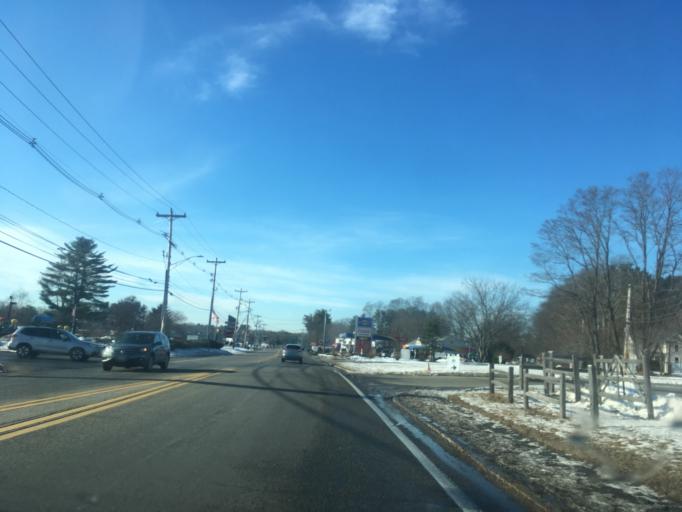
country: US
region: Massachusetts
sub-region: Essex County
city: Salisbury
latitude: 42.8442
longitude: -70.8933
